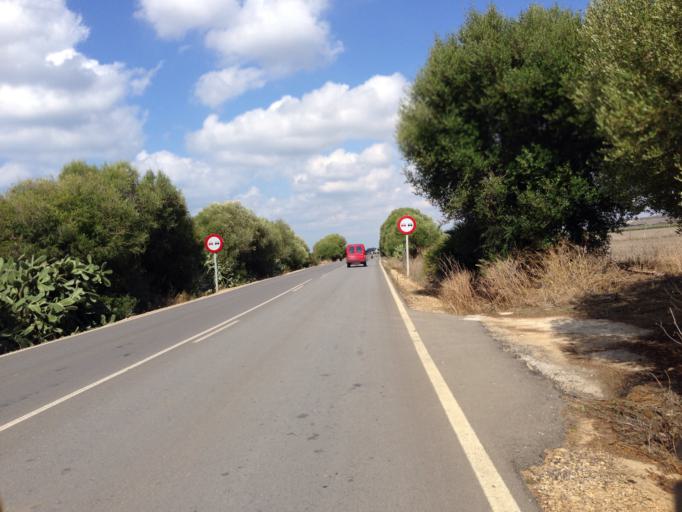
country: ES
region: Andalusia
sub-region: Provincia de Cadiz
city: Vejer de la Frontera
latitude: 36.2177
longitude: -6.0383
